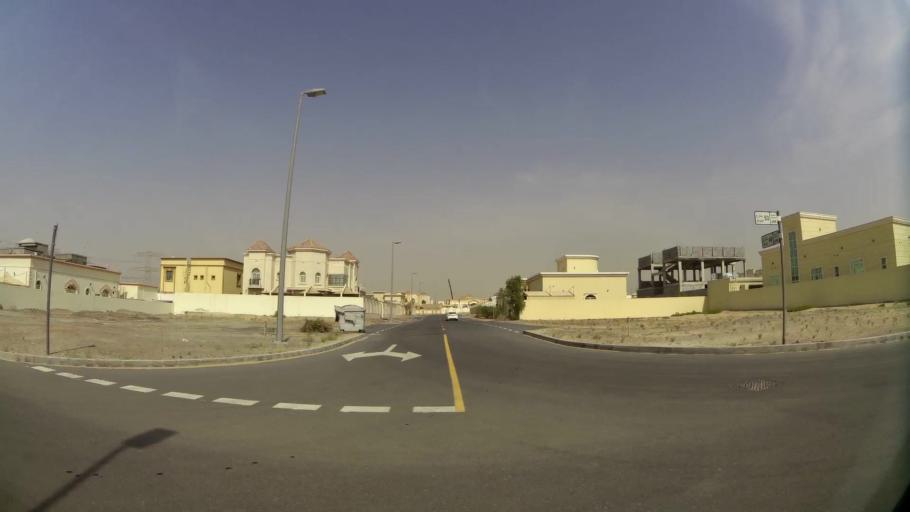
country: AE
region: Ash Shariqah
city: Sharjah
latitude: 25.2687
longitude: 55.4653
